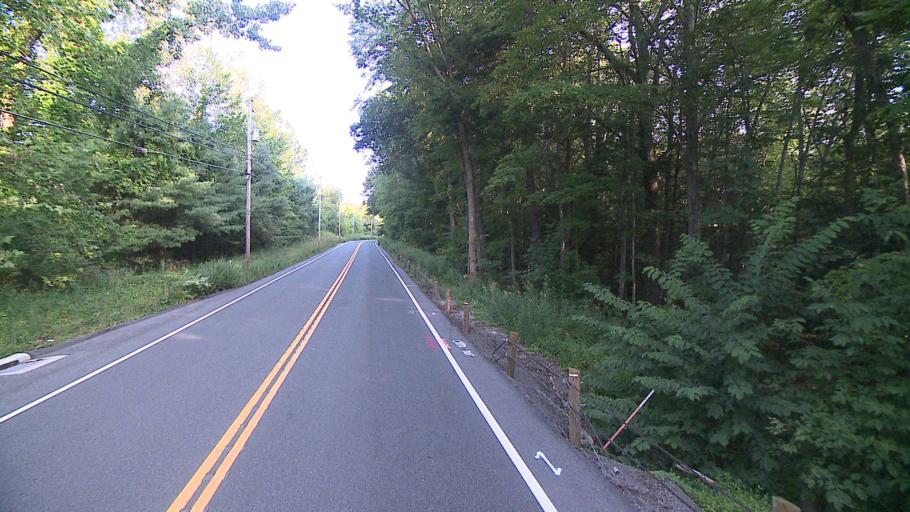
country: US
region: Connecticut
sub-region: Fairfield County
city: Sherman
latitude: 41.6212
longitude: -73.4628
